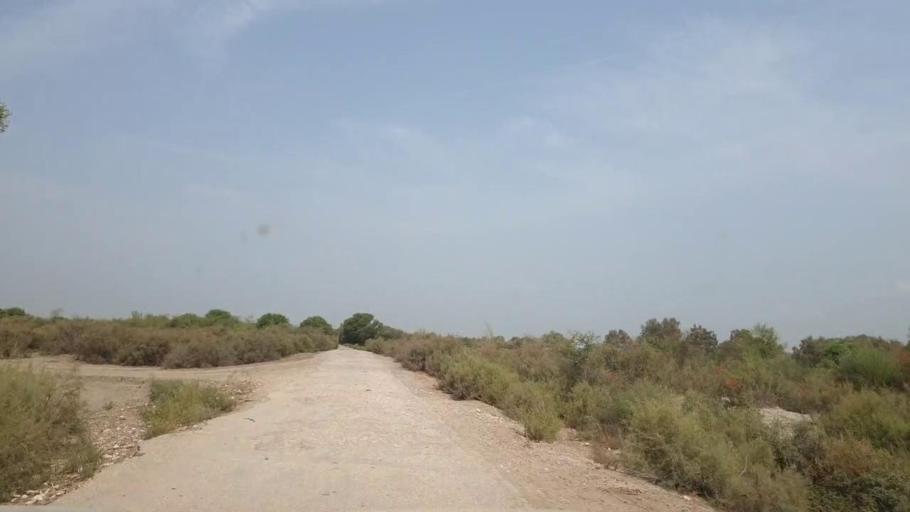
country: PK
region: Sindh
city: Sobhadero
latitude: 27.3941
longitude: 68.2631
